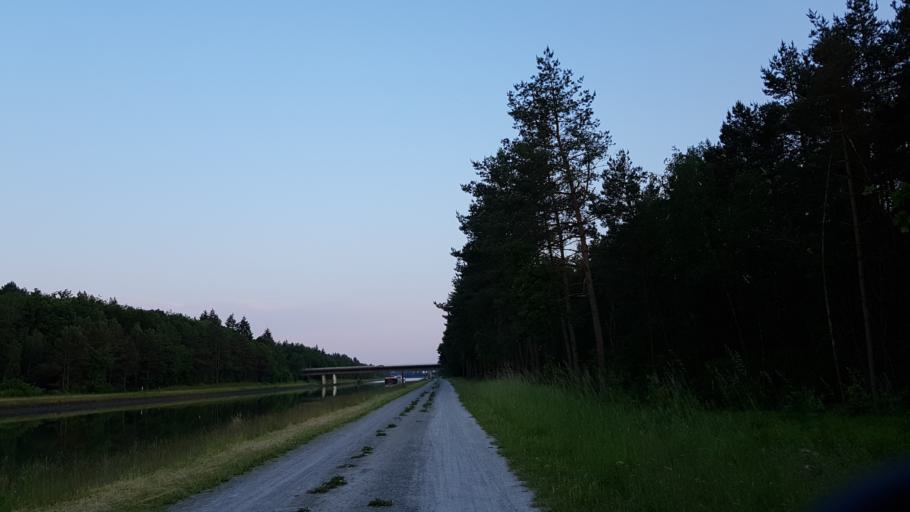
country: DE
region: Lower Saxony
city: Wendisch Evern
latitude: 53.2536
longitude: 10.4852
